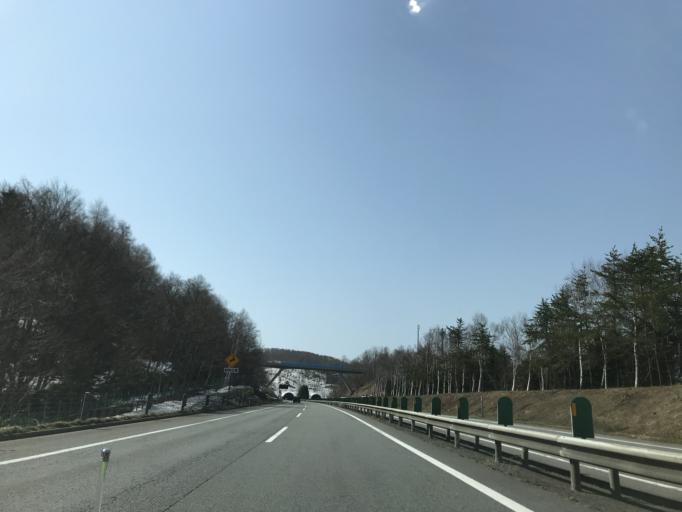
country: JP
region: Hokkaido
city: Bibai
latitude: 43.3134
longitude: 141.8825
